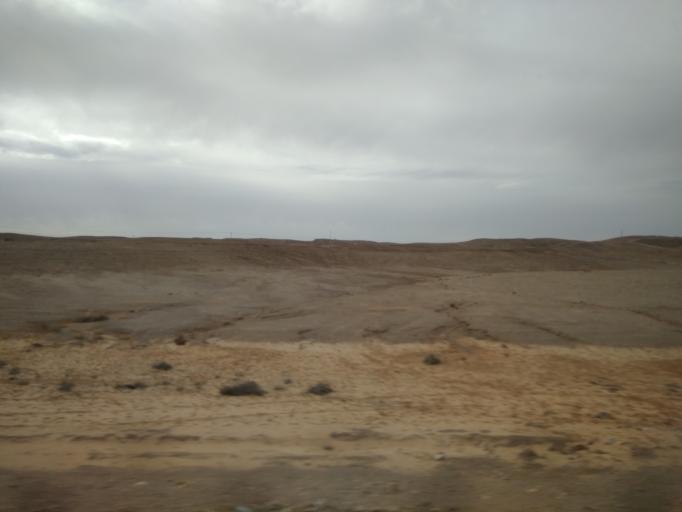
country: IL
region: Southern District
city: Eilat
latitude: 29.8984
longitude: 34.8600
